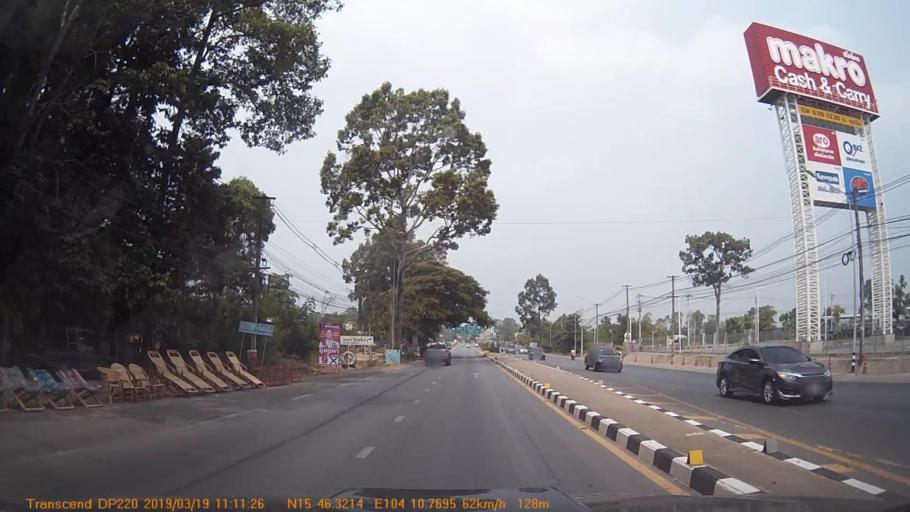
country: TH
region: Yasothon
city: Yasothon
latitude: 15.7722
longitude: 104.1792
